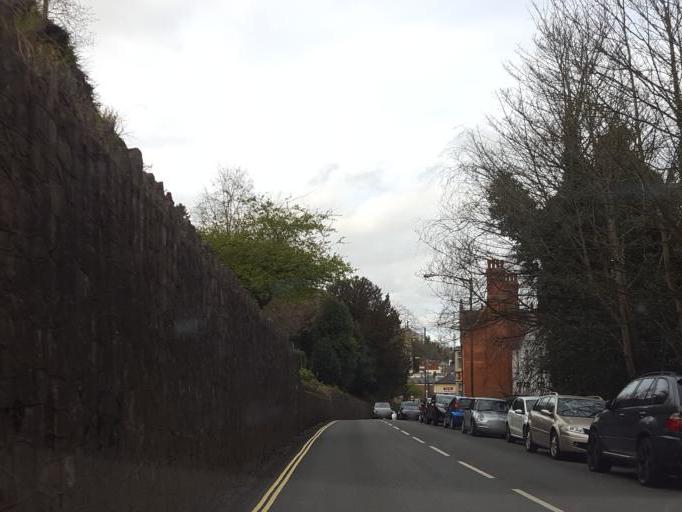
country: GB
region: England
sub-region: Worcestershire
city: Great Malvern
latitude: 52.1078
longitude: -2.3302
